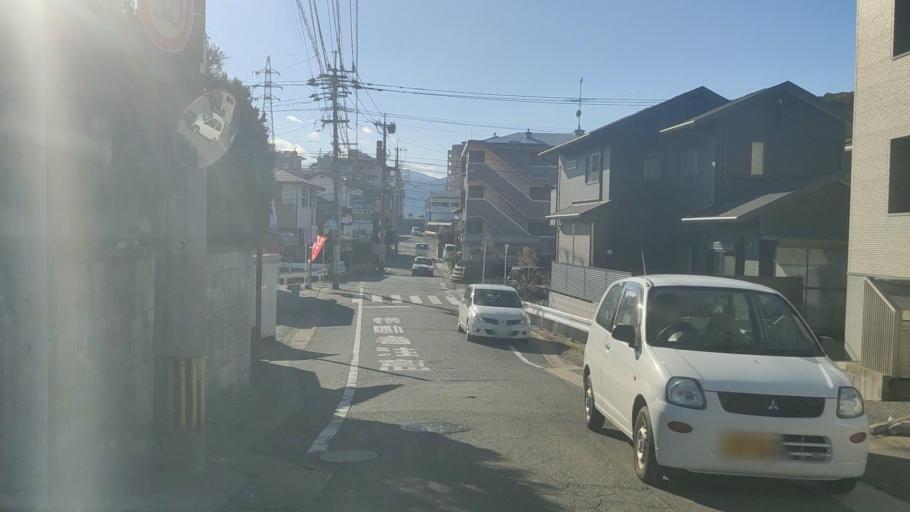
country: JP
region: Fukuoka
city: Fukuoka-shi
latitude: 33.5404
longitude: 130.3504
